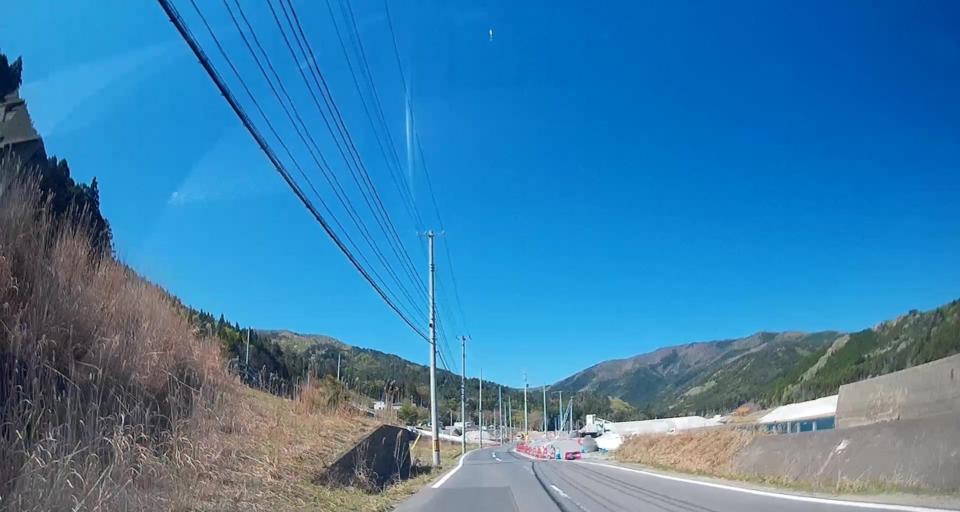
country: JP
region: Miyagi
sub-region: Oshika Gun
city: Onagawa Cho
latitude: 38.5139
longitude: 141.4684
